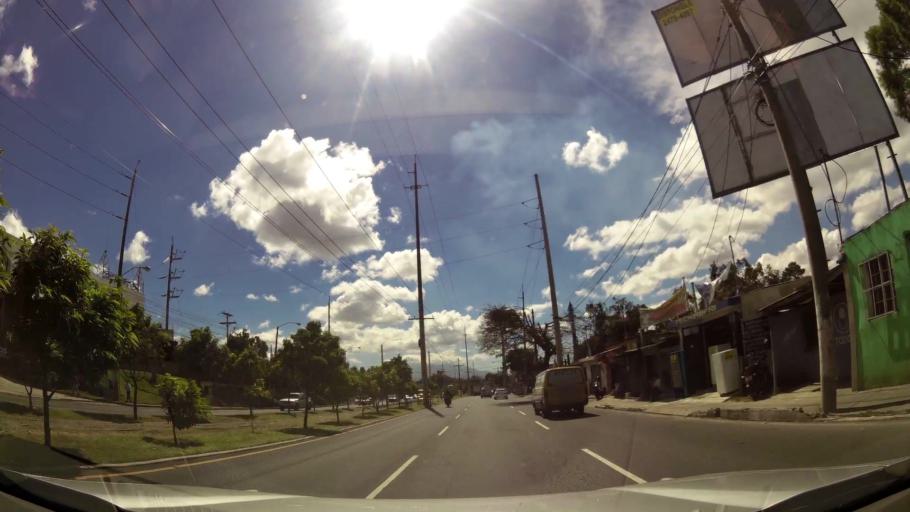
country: GT
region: Guatemala
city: Santa Catarina Pinula
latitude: 14.5622
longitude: -90.5463
